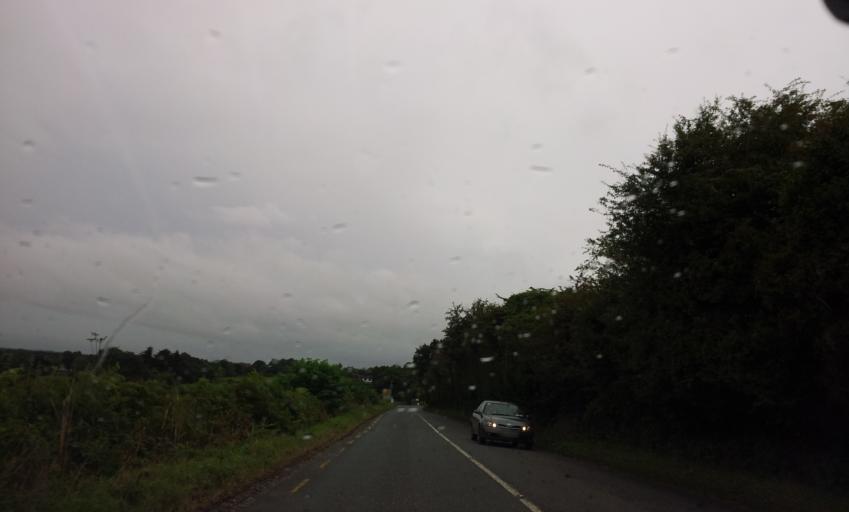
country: IE
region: Munster
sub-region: County Cork
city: Mallow
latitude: 52.2375
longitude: -8.4757
